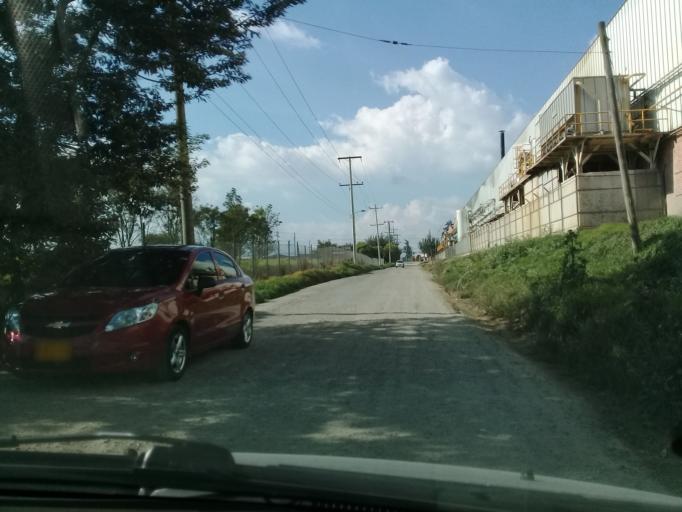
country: CO
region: Cundinamarca
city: Funza
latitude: 4.7299
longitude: -74.1845
